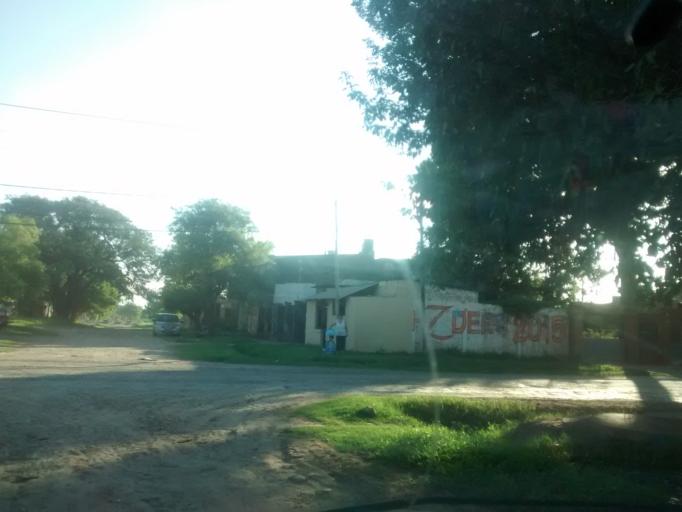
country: AR
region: Chaco
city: Resistencia
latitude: -27.4327
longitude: -58.9927
